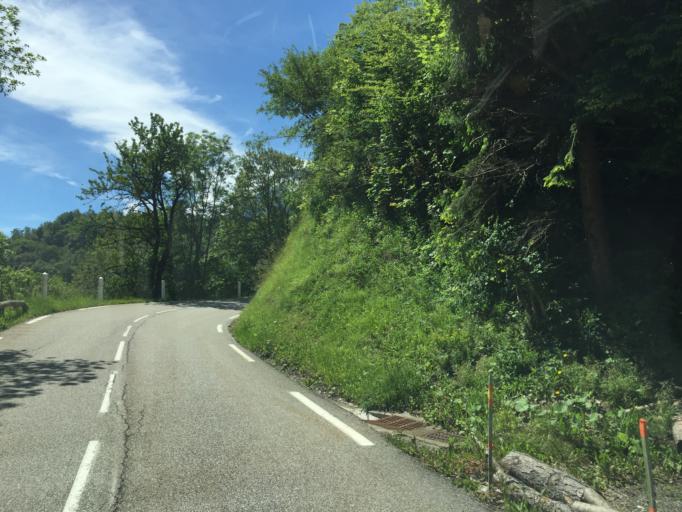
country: FR
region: Rhone-Alpes
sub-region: Departement de la Savoie
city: Saint-Baldoph
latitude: 45.5046
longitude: 5.9198
